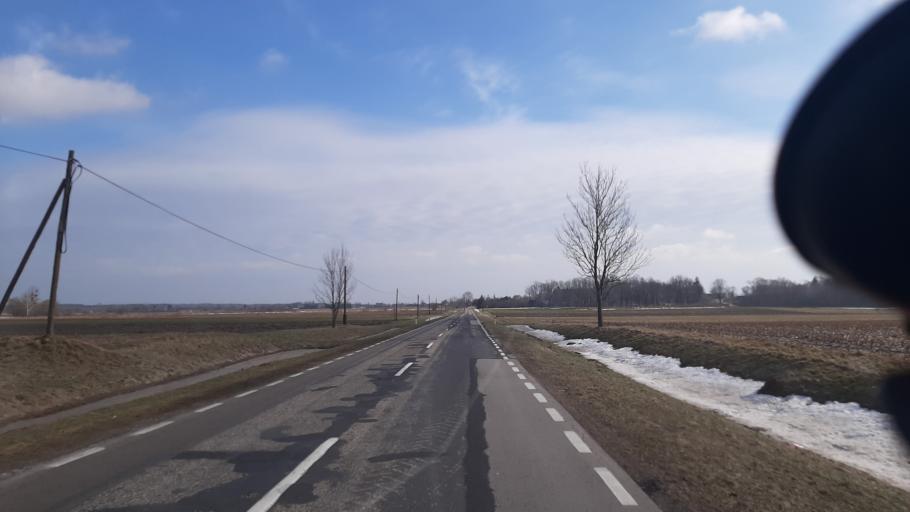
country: PL
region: Lublin Voivodeship
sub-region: Powiat wlodawski
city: Urszulin
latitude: 51.4895
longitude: 23.2773
